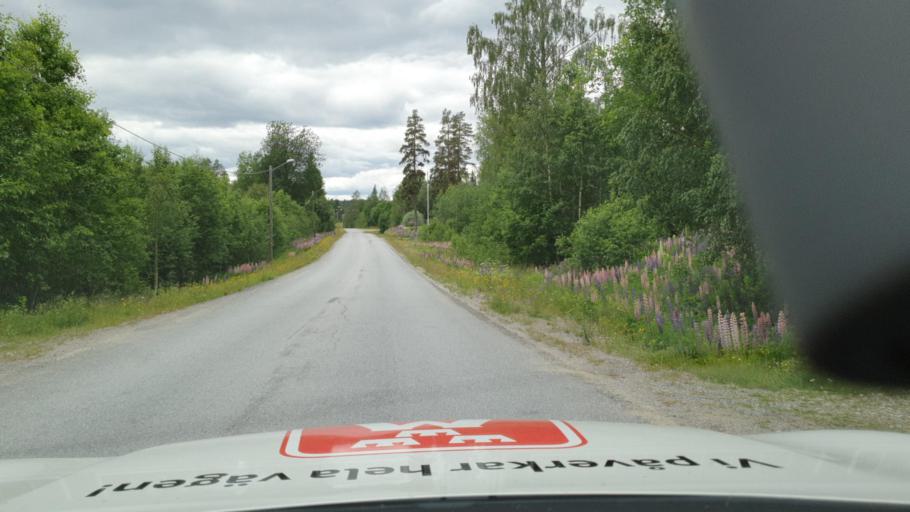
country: SE
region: Vaesterbotten
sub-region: Bjurholms Kommun
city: Bjurholm
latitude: 63.7863
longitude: 19.1798
